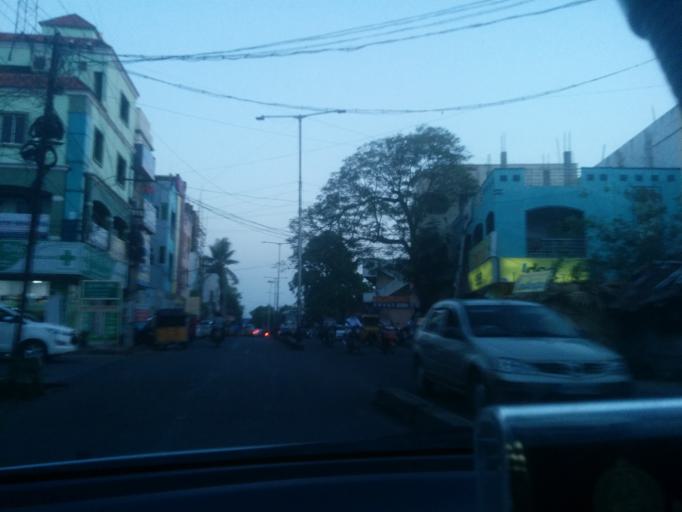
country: IN
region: Andhra Pradesh
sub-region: East Godavari
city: Rajahmundry
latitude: 17.0084
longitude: 81.7803
